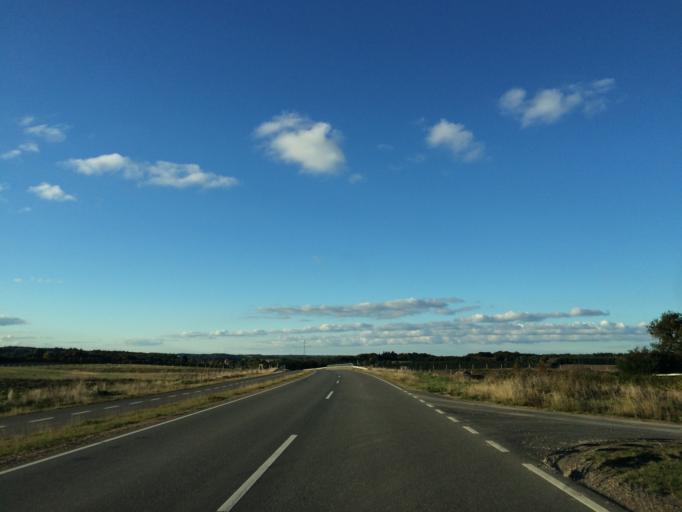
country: DK
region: Central Jutland
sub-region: Silkeborg Kommune
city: Svejbaek
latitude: 56.1458
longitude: 9.7055
